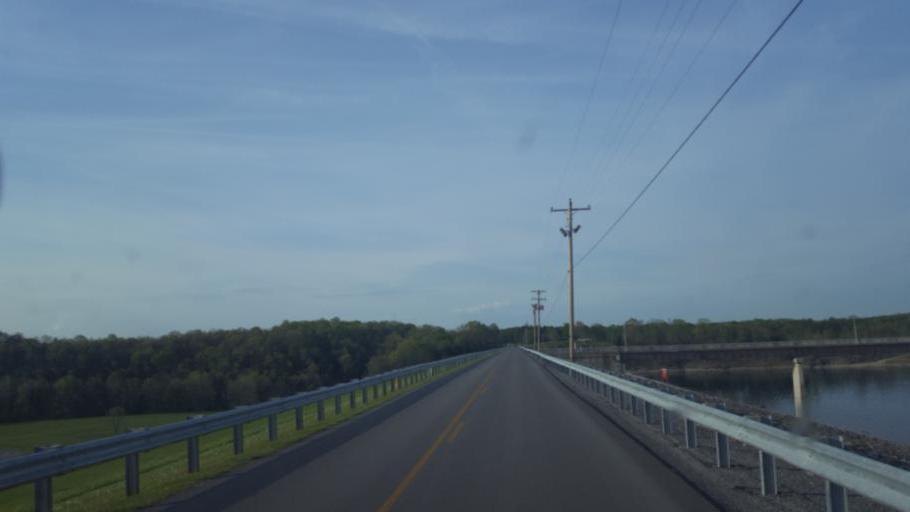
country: US
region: Kentucky
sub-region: Allen County
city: Scottsville
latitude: 36.8914
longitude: -86.1263
